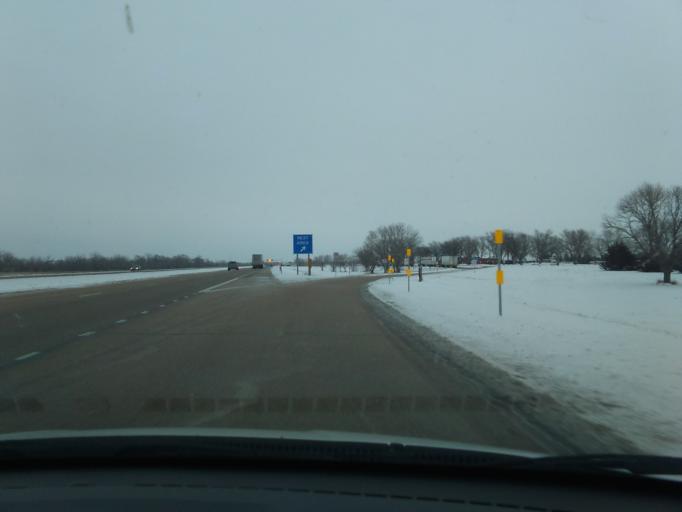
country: US
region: Nebraska
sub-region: Keith County
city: Ogallala
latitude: 41.1066
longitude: -101.7604
